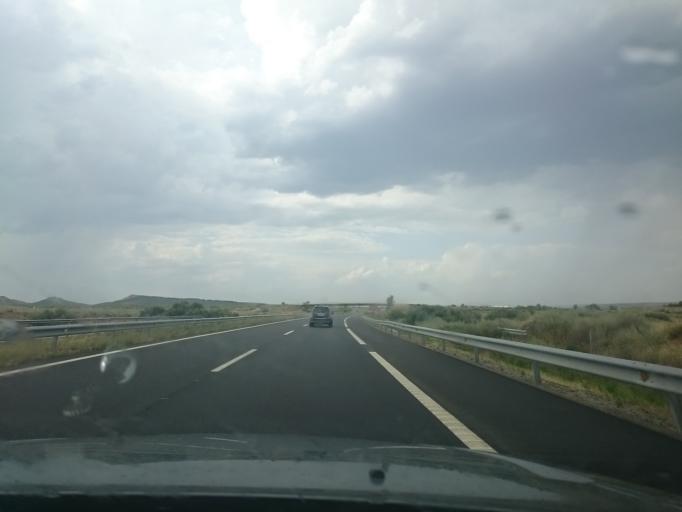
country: ES
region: La Rioja
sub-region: Provincia de La Rioja
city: Aldeanueva de Ebro
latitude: 42.2579
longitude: -1.9226
